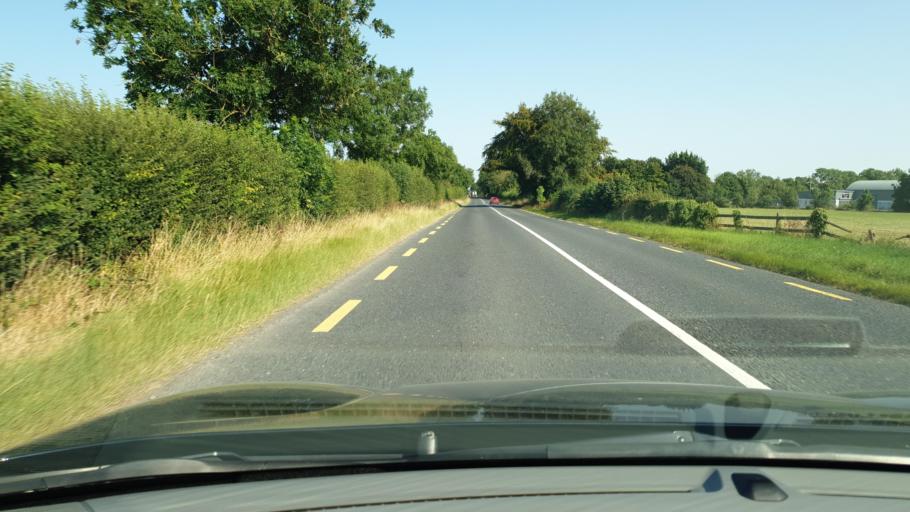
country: IE
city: Kentstown
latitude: 53.6315
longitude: -6.5535
